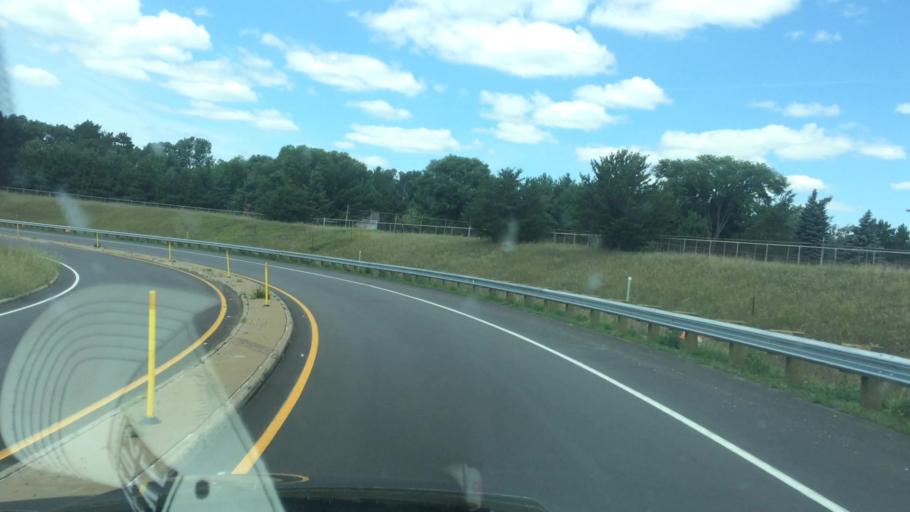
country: US
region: Wisconsin
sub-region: Portage County
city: Whiting
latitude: 44.5252
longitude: -89.5258
